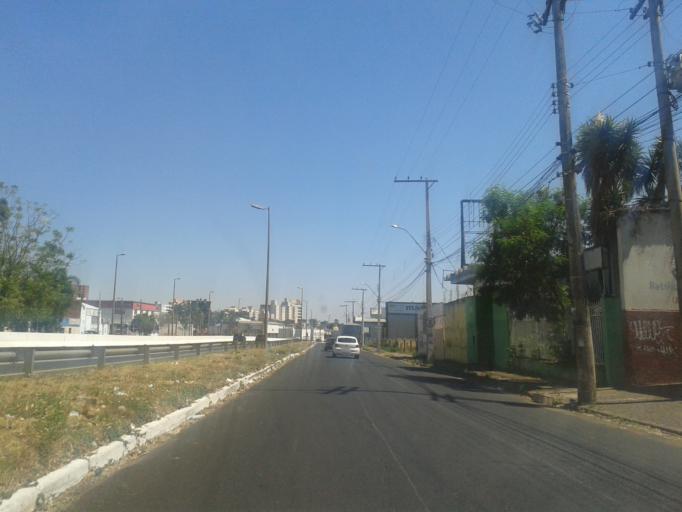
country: BR
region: Minas Gerais
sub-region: Uberlandia
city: Uberlandia
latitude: -18.9010
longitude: -48.2756
